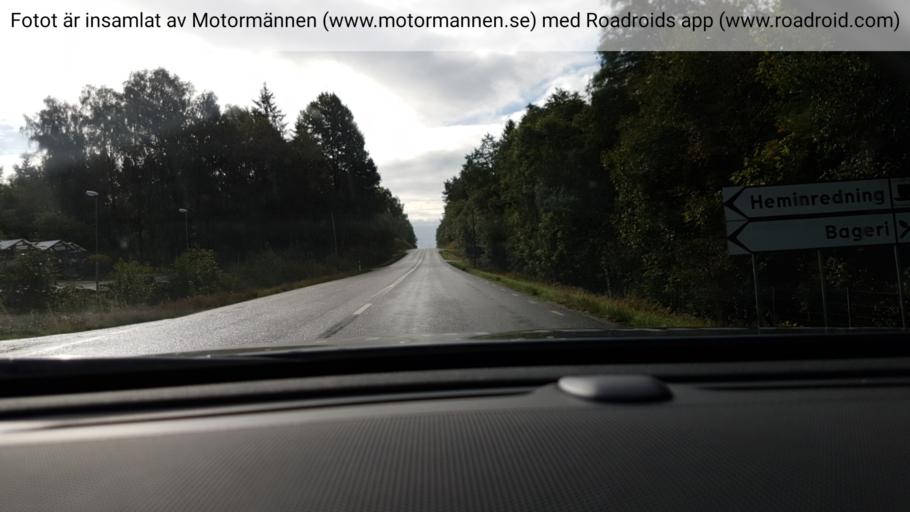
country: SE
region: Vaestra Goetaland
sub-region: Harryda Kommun
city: Ravlanda
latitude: 57.5671
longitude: 12.5110
